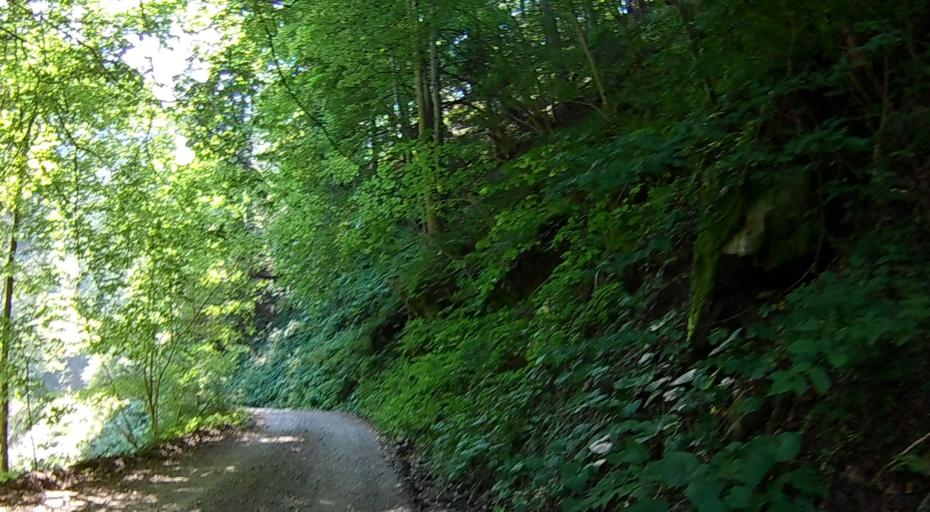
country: SI
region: Selnica ob Dravi
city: Selnica ob Dravi
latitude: 46.5159
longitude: 15.4565
